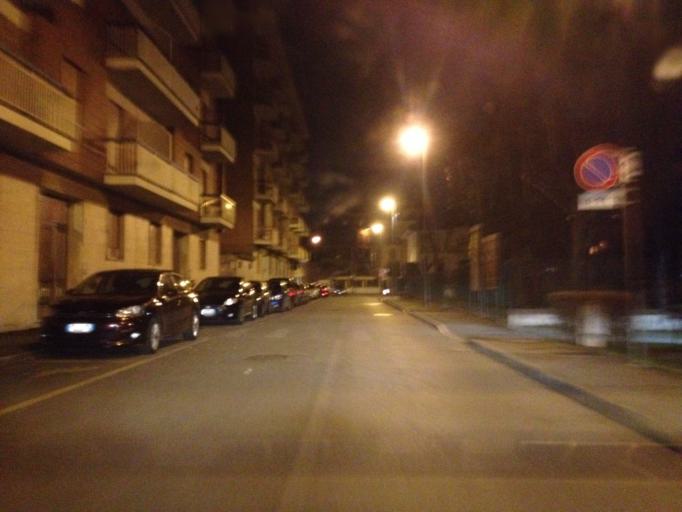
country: IT
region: Piedmont
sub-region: Provincia di Torino
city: Settimo Torinese
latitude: 45.1339
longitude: 7.7681
